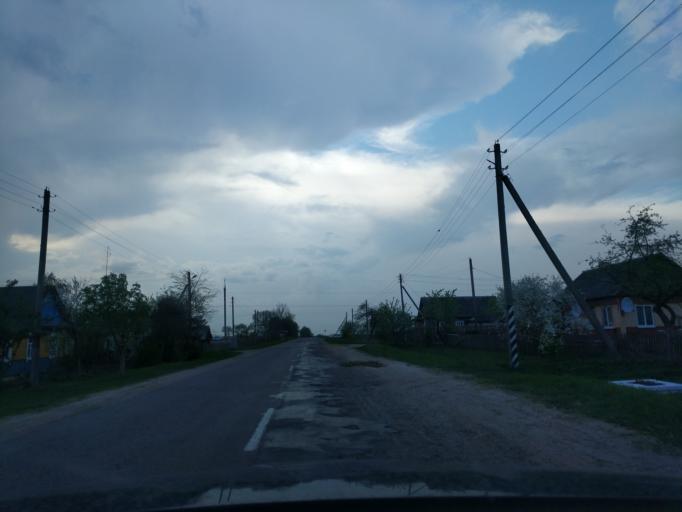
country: BY
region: Minsk
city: Novy Svyerzhan'
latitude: 53.4715
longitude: 26.6402
